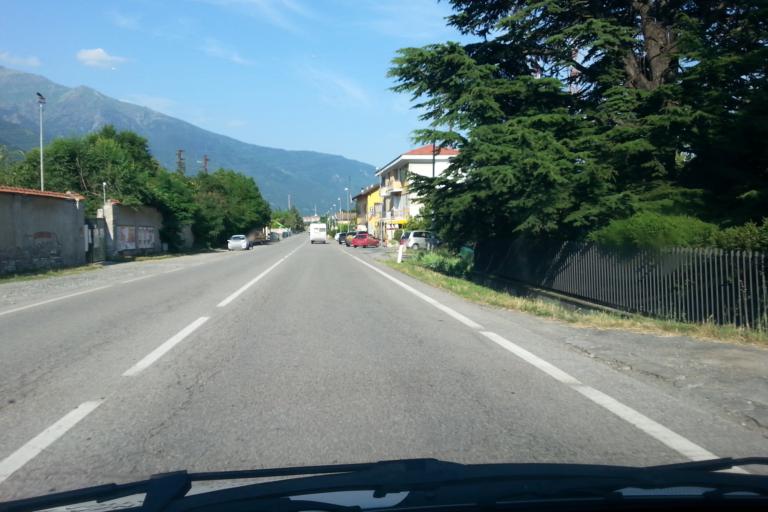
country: IT
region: Piedmont
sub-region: Provincia di Torino
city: Bussoleno
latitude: 45.1379
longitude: 7.1261
